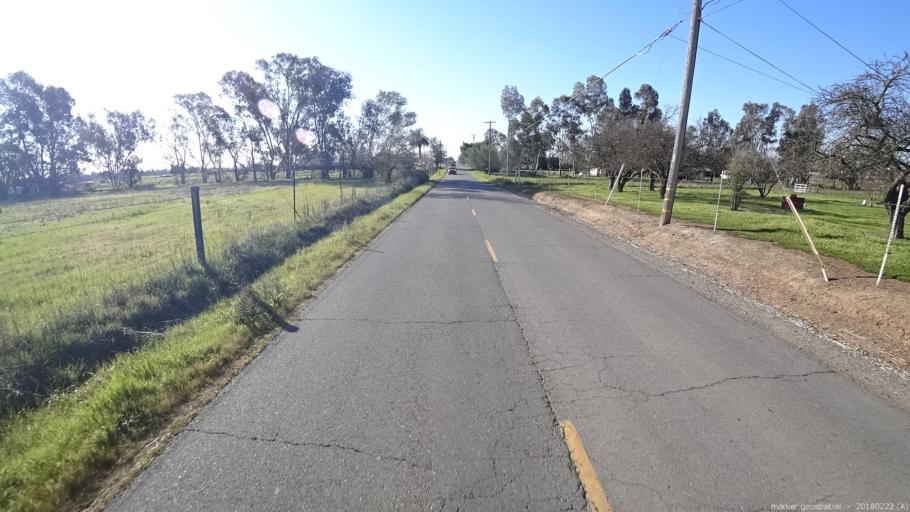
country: US
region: California
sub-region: Sacramento County
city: Elverta
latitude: 38.7250
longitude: -121.4668
